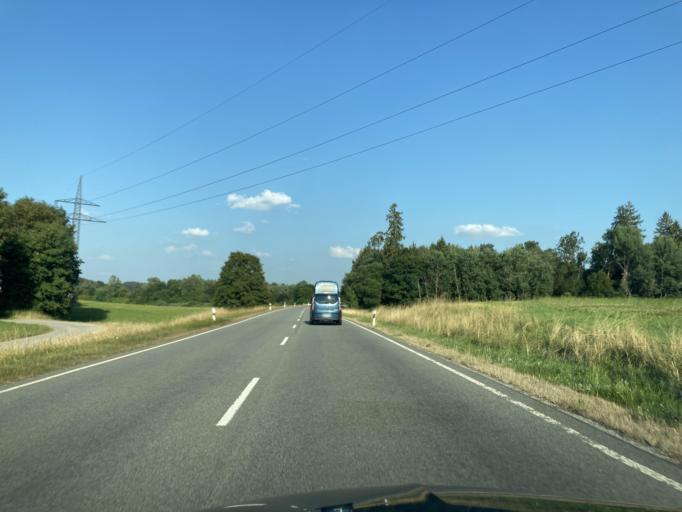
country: DE
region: Bavaria
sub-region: Upper Bavaria
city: Babensham
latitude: 48.0583
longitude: 12.2664
